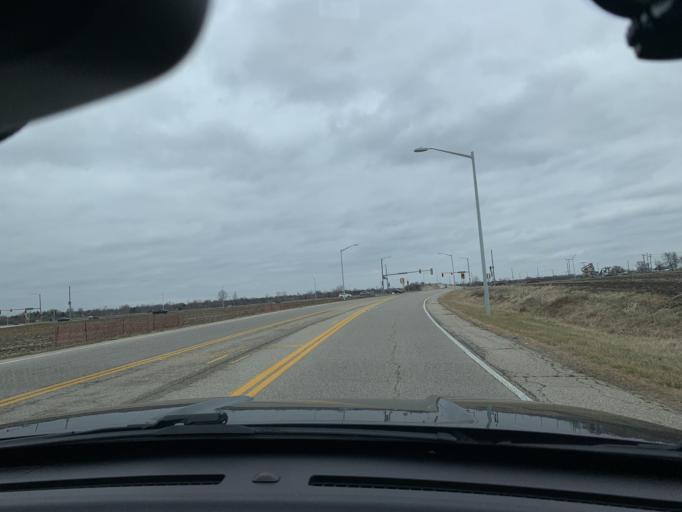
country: US
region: Illinois
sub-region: Sangamon County
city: Jerome
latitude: 39.7362
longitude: -89.6904
